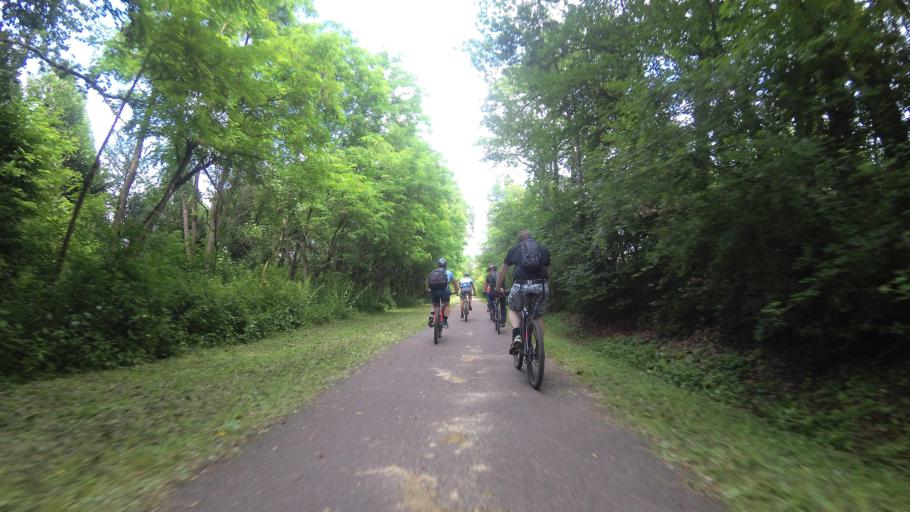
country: FR
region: Lorraine
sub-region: Departement de la Moselle
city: Bliesbruck
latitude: 49.1216
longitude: 7.1409
